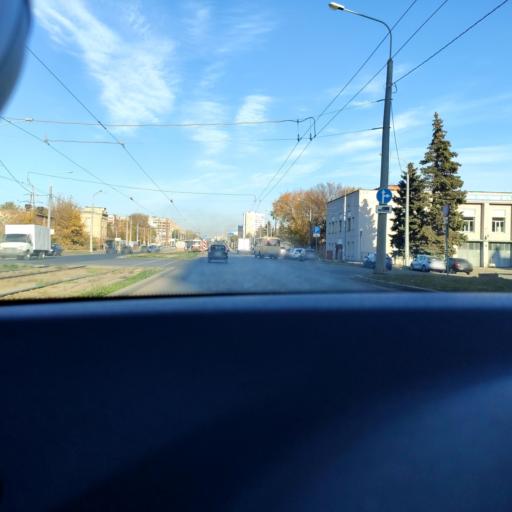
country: RU
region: Samara
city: Samara
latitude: 53.2051
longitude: 50.2715
